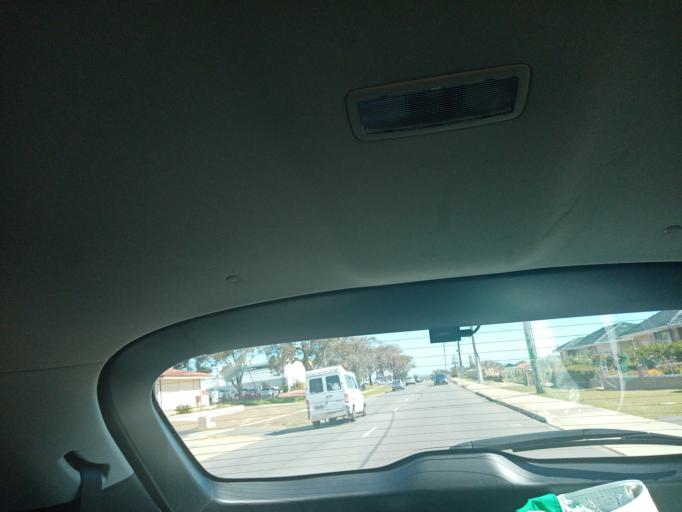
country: AU
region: Western Australia
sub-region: City of Cockburn
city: Spearwood
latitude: -32.1139
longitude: 115.7827
